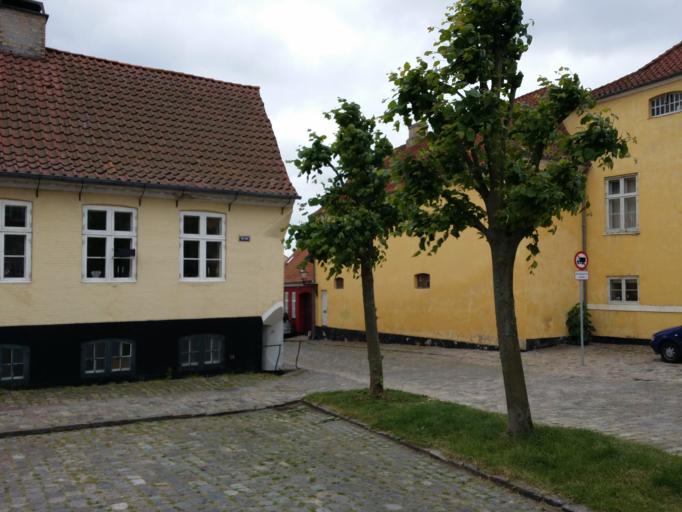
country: DK
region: Zealand
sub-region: Vordingborg Kommune
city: Praesto
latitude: 55.1237
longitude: 12.0443
